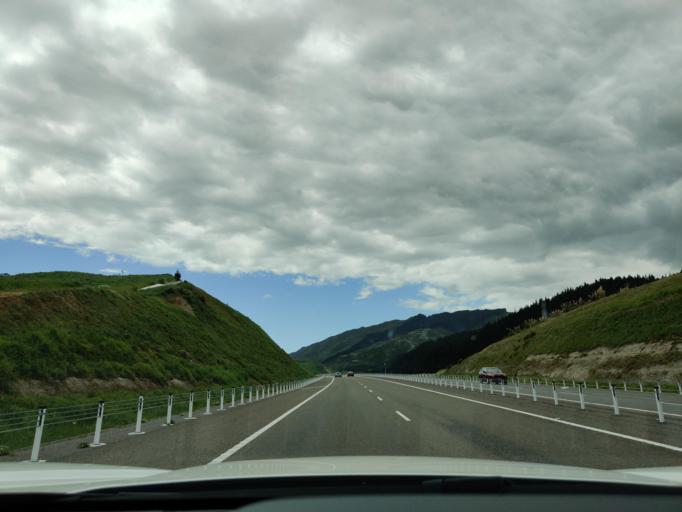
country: NZ
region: Wellington
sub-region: Porirua City
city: Porirua
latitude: -41.0648
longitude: 174.9437
